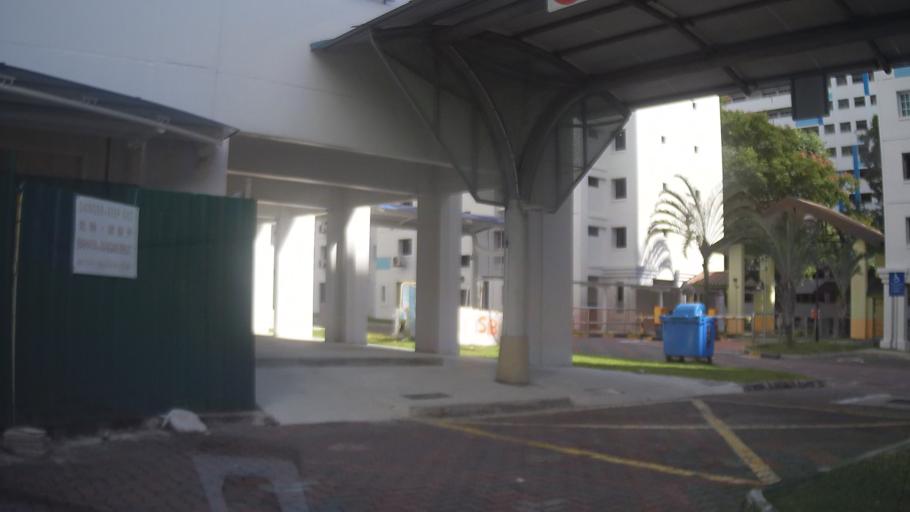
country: MY
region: Johor
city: Johor Bahru
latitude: 1.4270
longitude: 103.7732
